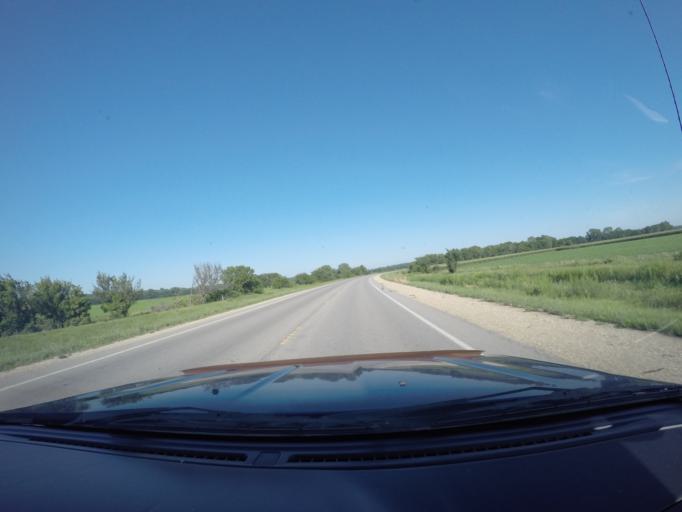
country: US
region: Kansas
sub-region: Jefferson County
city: Oskaloosa
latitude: 39.0866
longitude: -95.4150
